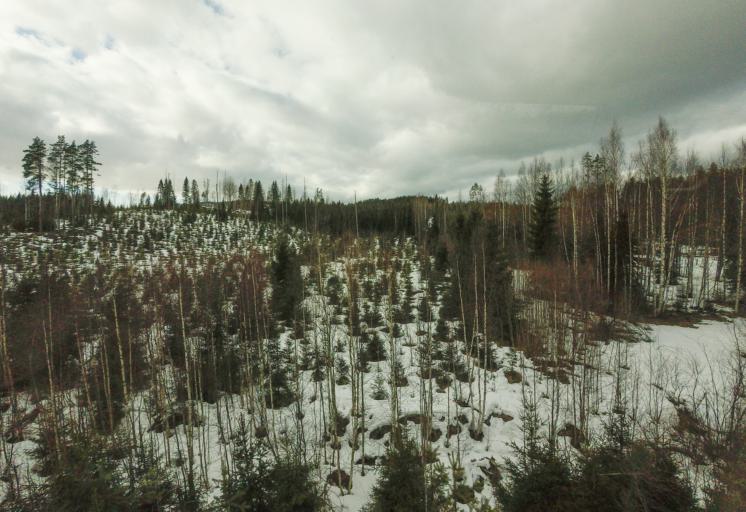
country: FI
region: South Karelia
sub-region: Imatra
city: Rautjaervi
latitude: 61.3096
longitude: 29.1083
